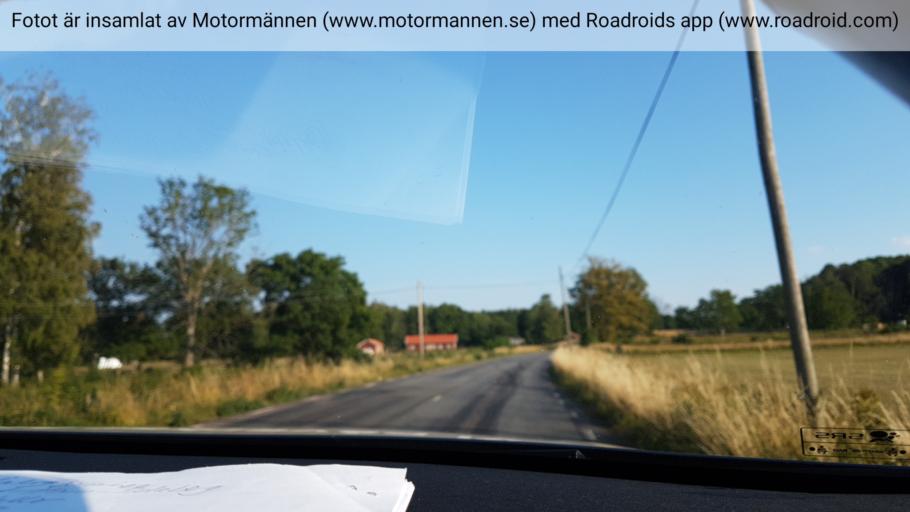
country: SE
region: Vaestra Goetaland
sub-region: Skovde Kommun
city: Stopen
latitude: 58.4850
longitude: 13.8371
